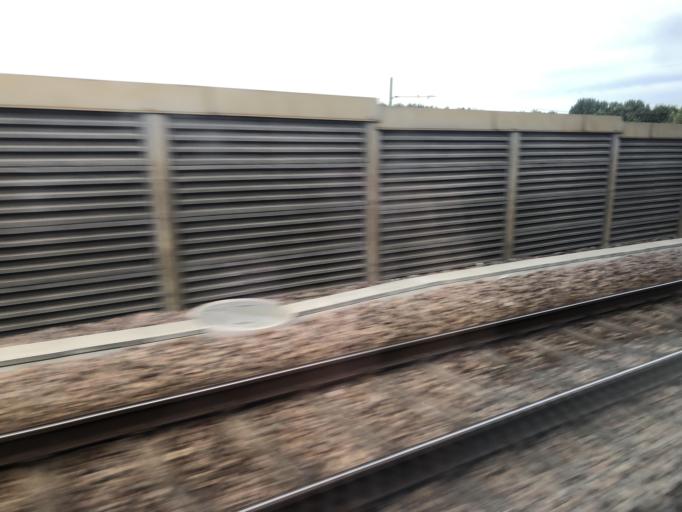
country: SE
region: Skane
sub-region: Burlovs Kommun
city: Arloev
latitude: 55.6301
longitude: 13.0623
